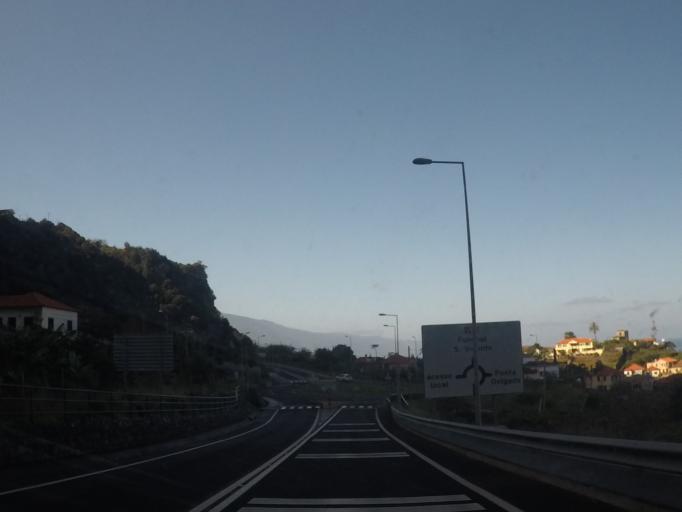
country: PT
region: Madeira
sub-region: Sao Vicente
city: Sao Vicente
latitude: 32.8215
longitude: -16.9891
